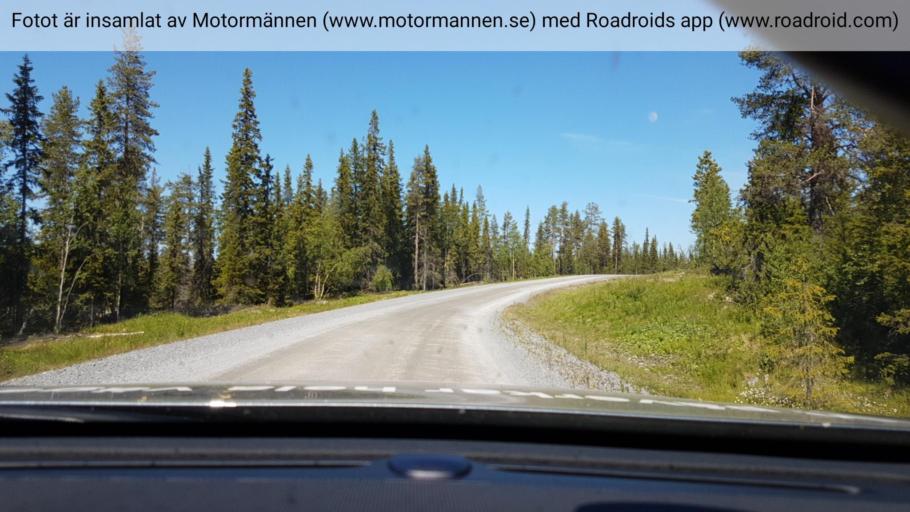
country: SE
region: Vaesterbotten
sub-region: Vilhelmina Kommun
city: Sjoberg
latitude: 64.6805
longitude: 15.7529
